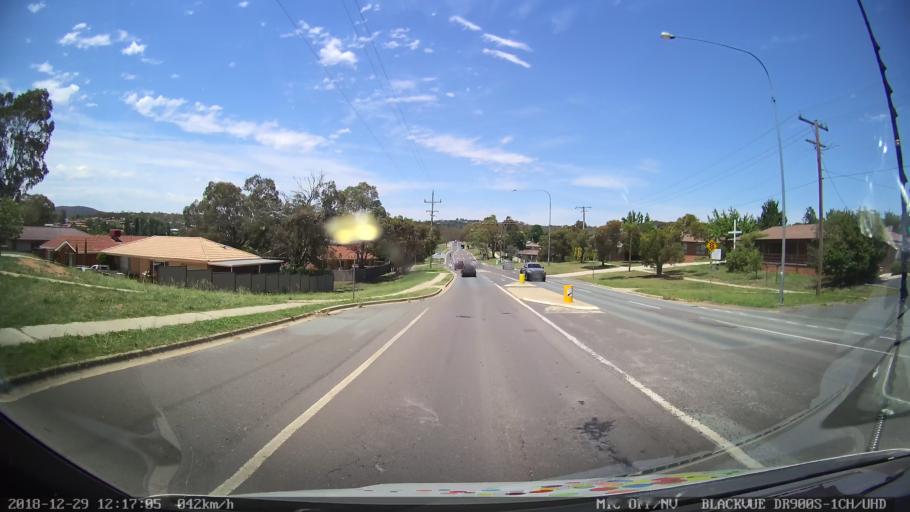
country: AU
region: New South Wales
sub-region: Queanbeyan
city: Queanbeyan
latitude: -35.3725
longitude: 149.2334
